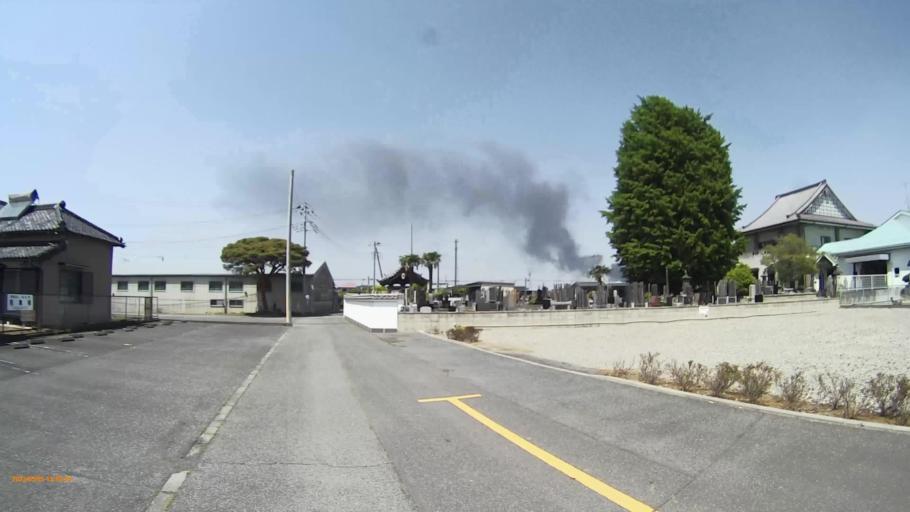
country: JP
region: Saitama
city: Kasukabe
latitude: 35.9548
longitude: 139.7774
